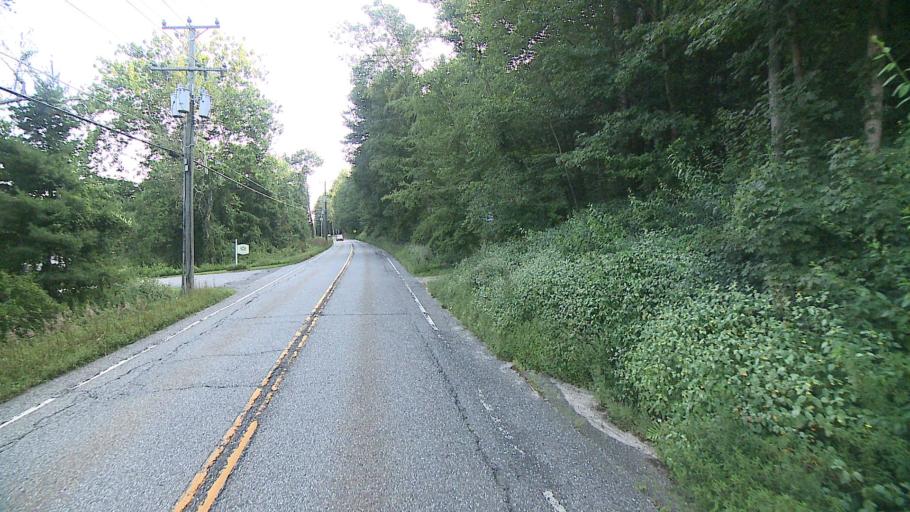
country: US
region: Connecticut
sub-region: Litchfield County
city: Kent
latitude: 41.7942
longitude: -73.3969
